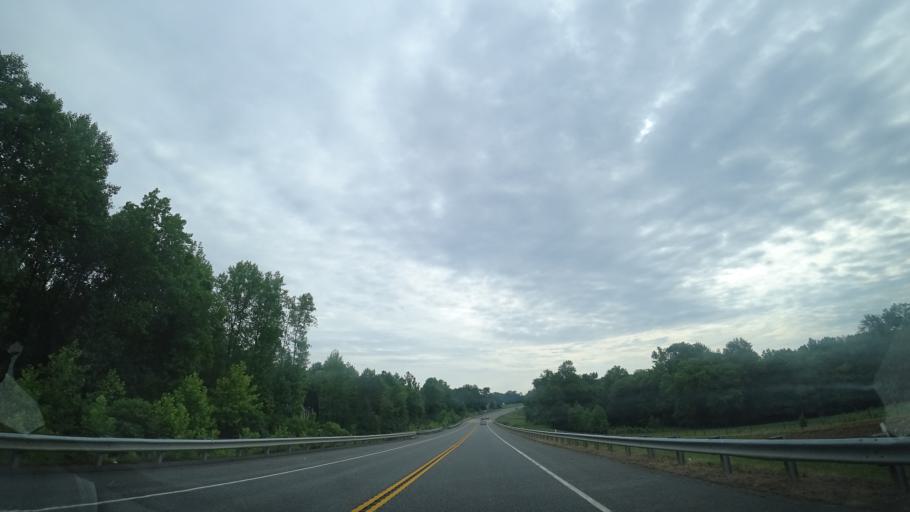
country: US
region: Virginia
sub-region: Spotsylvania County
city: Spotsylvania Courthouse
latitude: 38.1582
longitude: -77.6737
